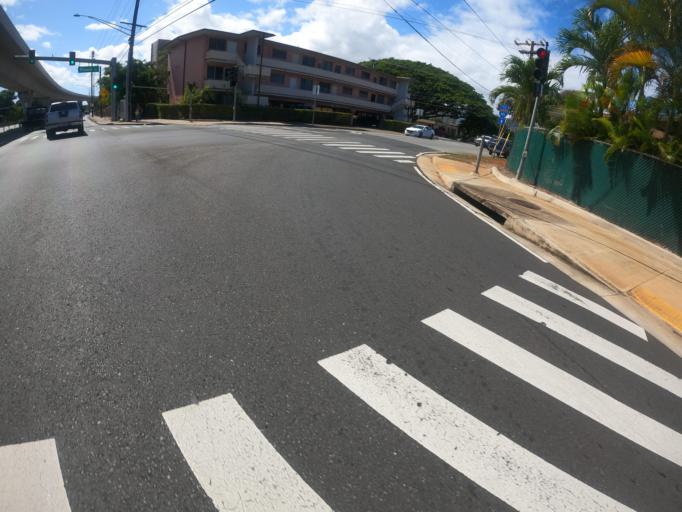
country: US
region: Hawaii
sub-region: Honolulu County
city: Waipahu
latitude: 21.3869
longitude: -157.9982
